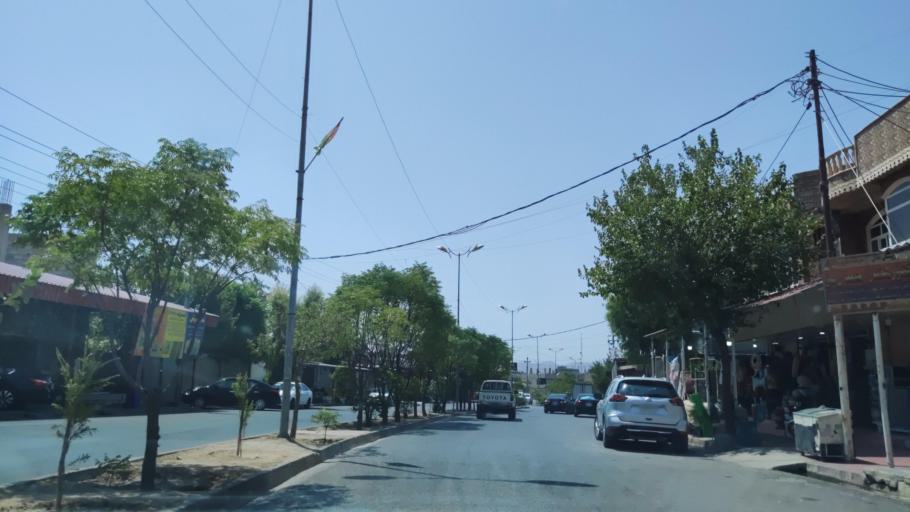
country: IQ
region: Arbil
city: Shaqlawah
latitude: 36.5513
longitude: 44.3549
